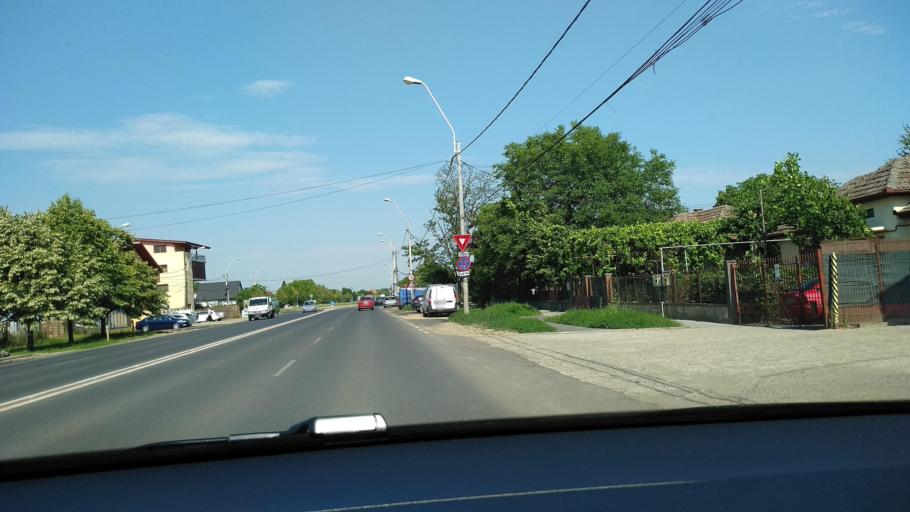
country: RO
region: Timis
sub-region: Comuna Ghiroda
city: Ghiroda
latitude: 45.7266
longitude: 21.2788
